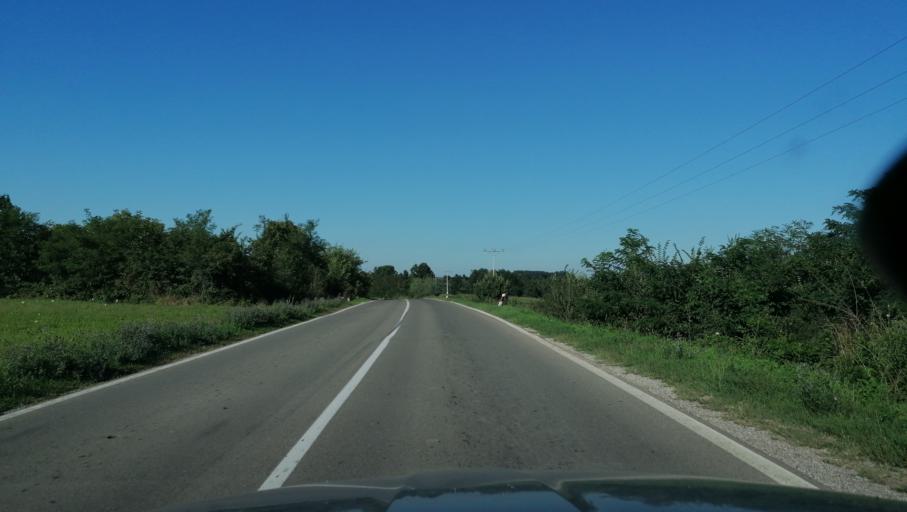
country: RS
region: Central Serbia
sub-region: Sumadijski Okrug
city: Knic
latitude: 43.8931
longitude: 20.6158
